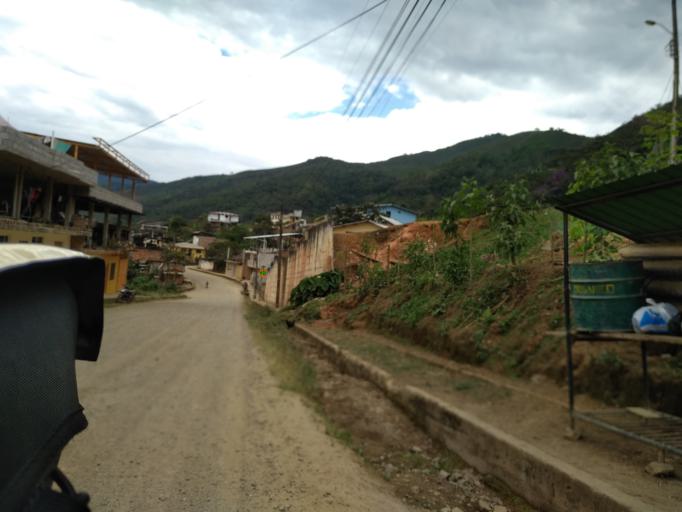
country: PE
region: Cajamarca
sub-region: Provincia de San Ignacio
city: Namballe
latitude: -4.8630
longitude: -79.1284
